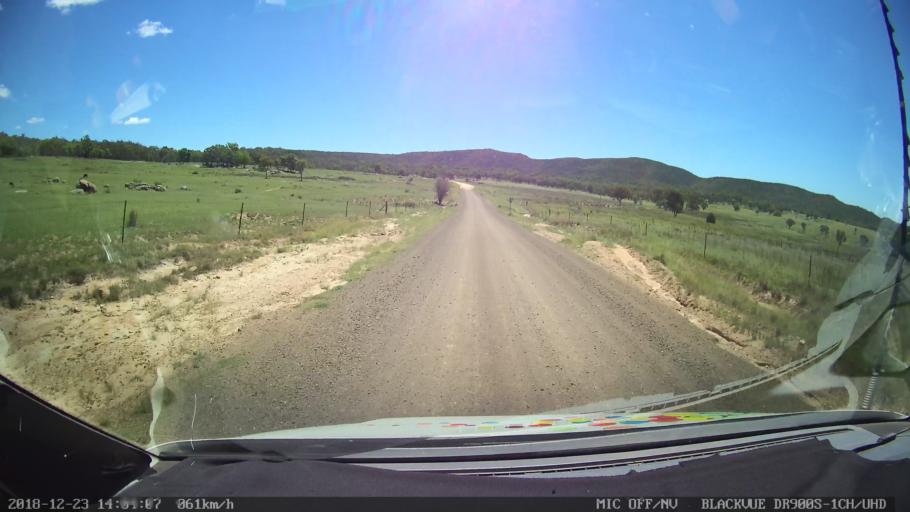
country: AU
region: New South Wales
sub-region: Tamworth Municipality
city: Manilla
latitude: -30.6222
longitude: 151.0937
